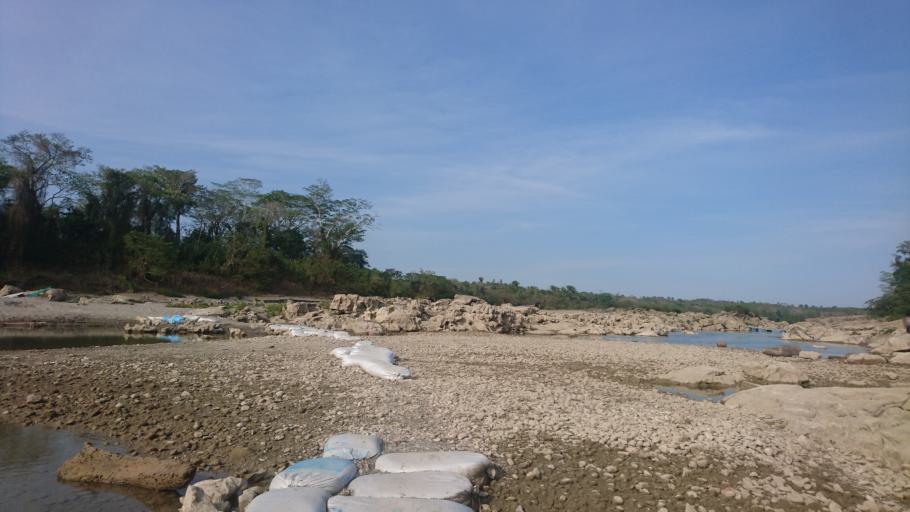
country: MX
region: Chiapas
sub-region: Ocosingo
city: Frontera Corozal
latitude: 16.8241
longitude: -90.8866
